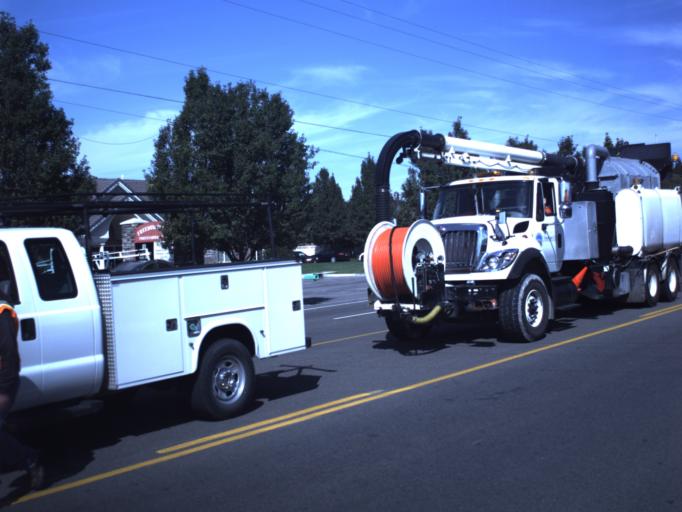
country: US
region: Utah
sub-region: Utah County
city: American Fork
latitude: 40.3716
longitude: -111.7691
